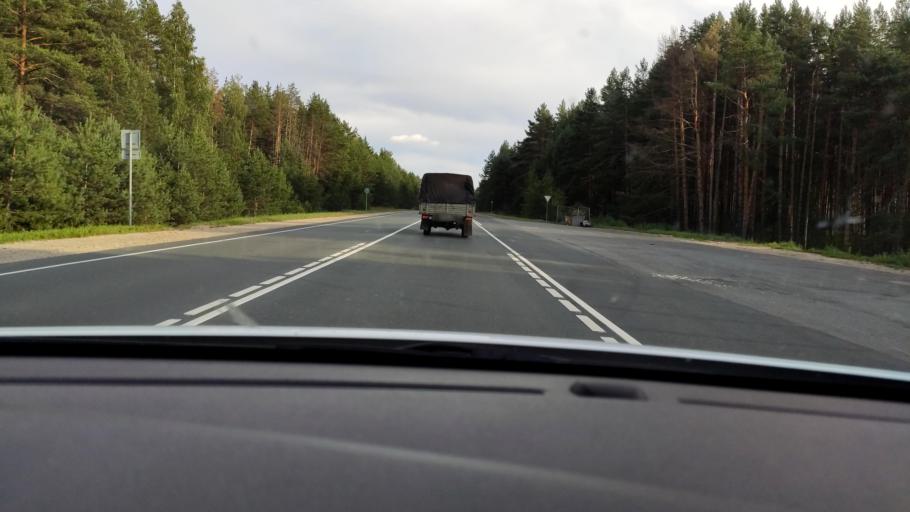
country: RU
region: Mariy-El
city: Krasnogorskiy
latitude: 56.0742
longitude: 48.3607
